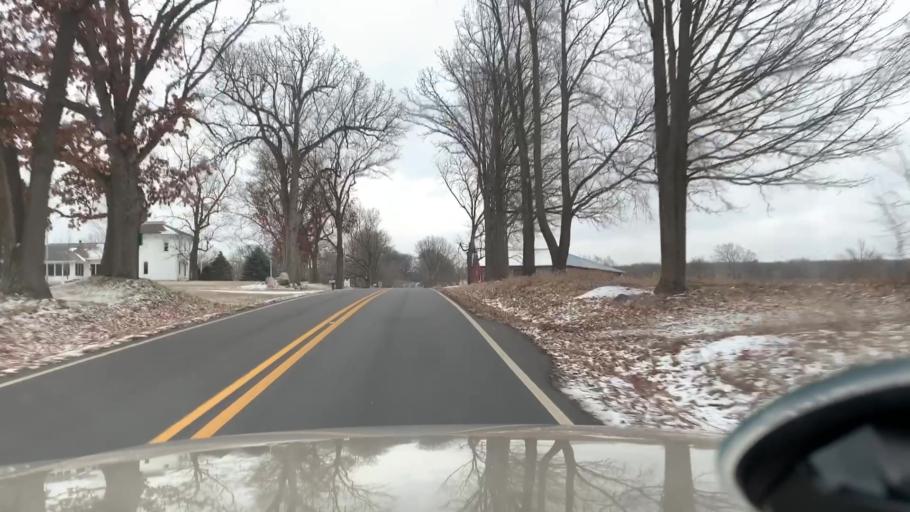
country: US
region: Michigan
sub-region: Jackson County
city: Spring Arbor
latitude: 42.2008
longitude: -84.5299
